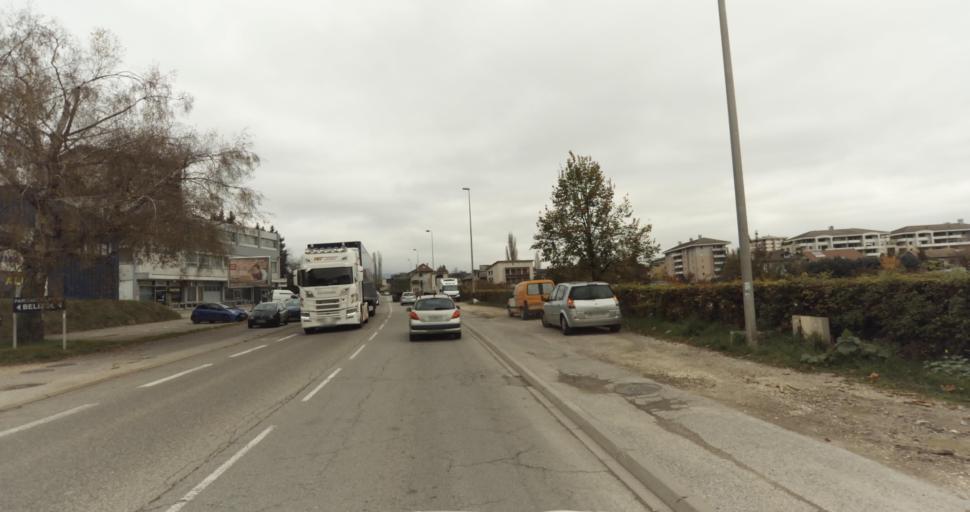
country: FR
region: Rhone-Alpes
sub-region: Departement de la Haute-Savoie
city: Annecy
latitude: 45.8932
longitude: 6.1141
